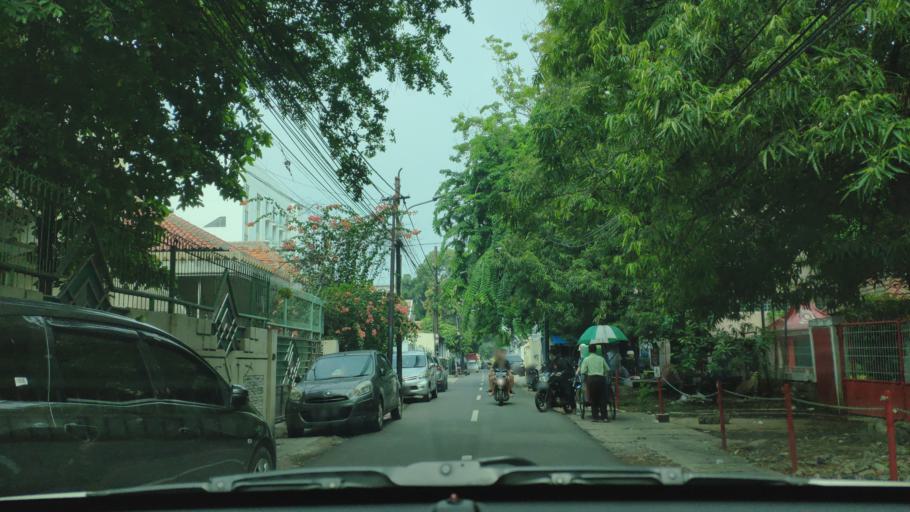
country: ID
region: Jakarta Raya
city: Jakarta
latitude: -6.1631
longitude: 106.8154
